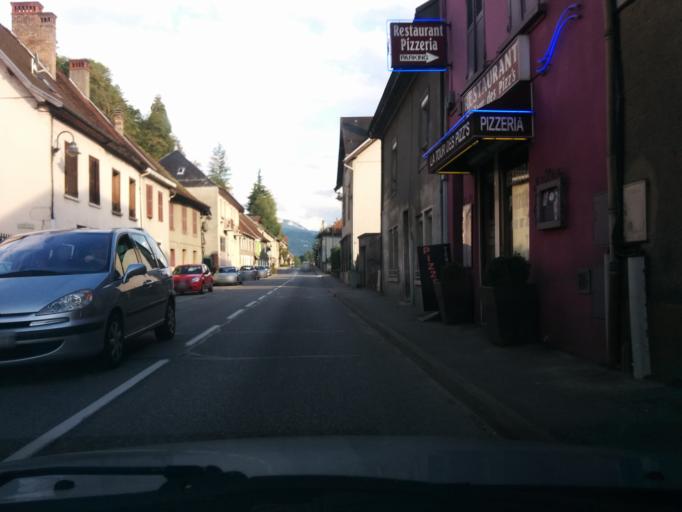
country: FR
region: Rhone-Alpes
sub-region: Departement de la Savoie
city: Le Pont-de-Beauvoisin
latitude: 45.5344
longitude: 5.6759
